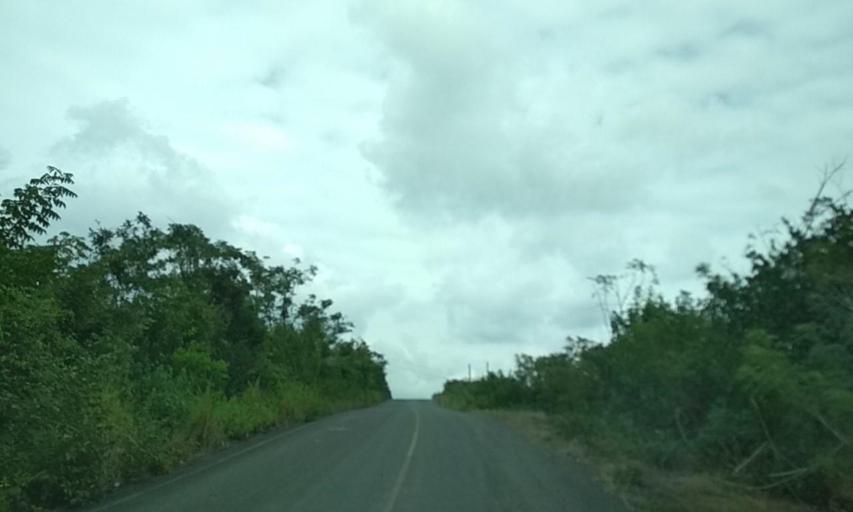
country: MX
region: Veracruz
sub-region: Papantla
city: El Chote
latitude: 20.3488
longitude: -97.3848
